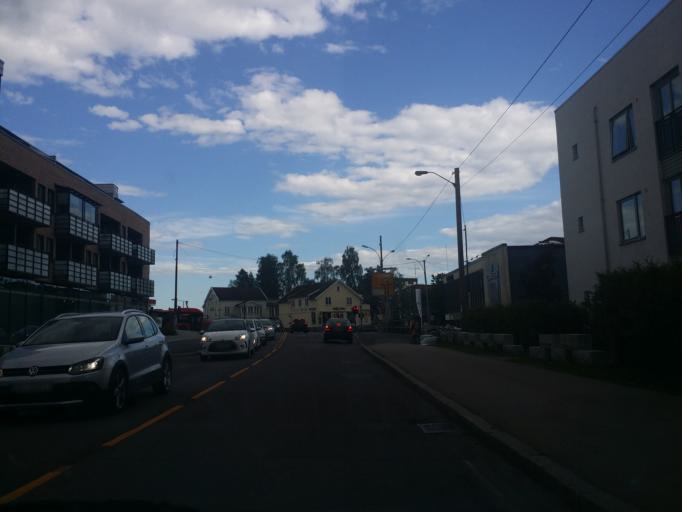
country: NO
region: Akershus
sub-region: Baerum
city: Lysaker
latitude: 59.9482
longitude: 10.6418
